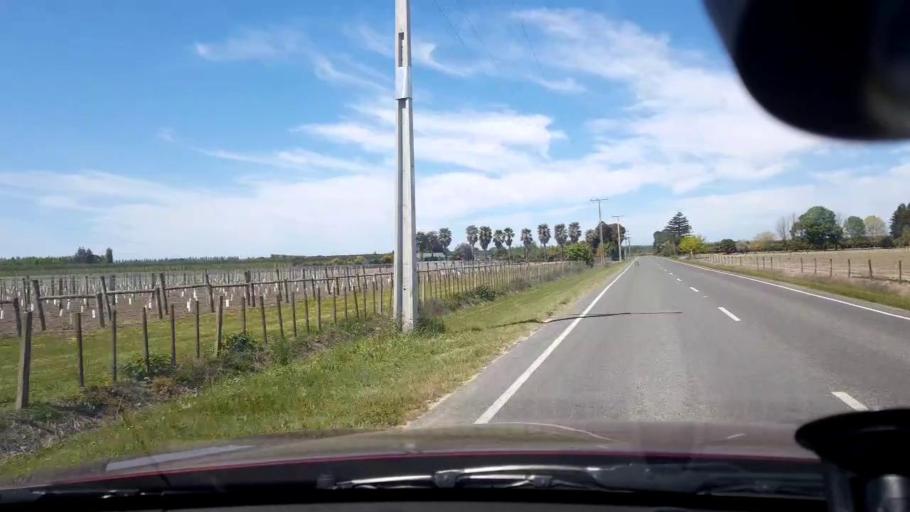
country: NZ
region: Gisborne
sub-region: Gisborne District
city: Gisborne
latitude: -38.6348
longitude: 177.9296
